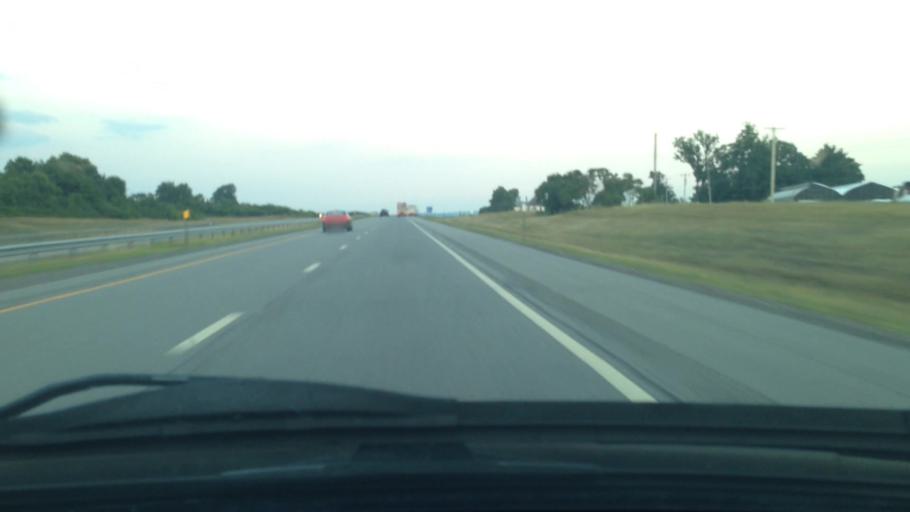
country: US
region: New York
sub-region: Montgomery County
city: Fort Plain
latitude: 42.9632
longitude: -74.6409
